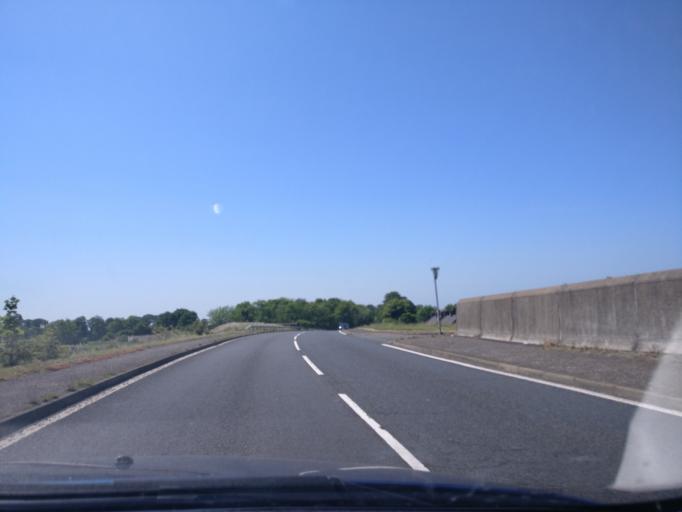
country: GB
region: Scotland
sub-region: East Lothian
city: Longniddry
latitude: 55.9845
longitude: -2.8528
